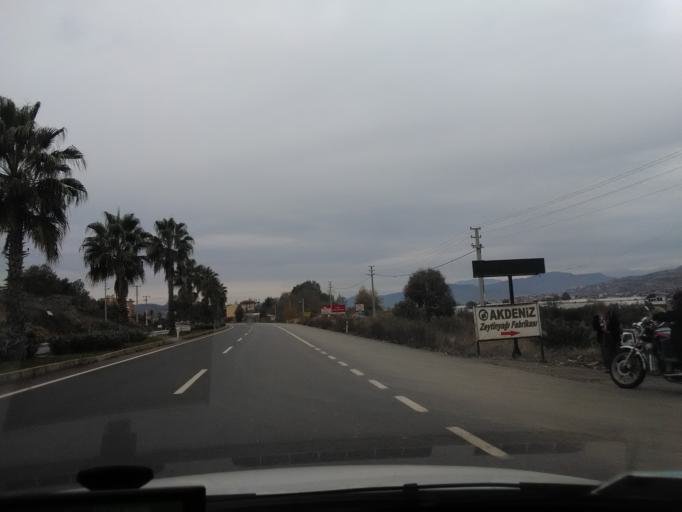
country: TR
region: Antalya
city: Gazipasa
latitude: 36.2526
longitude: 32.3371
